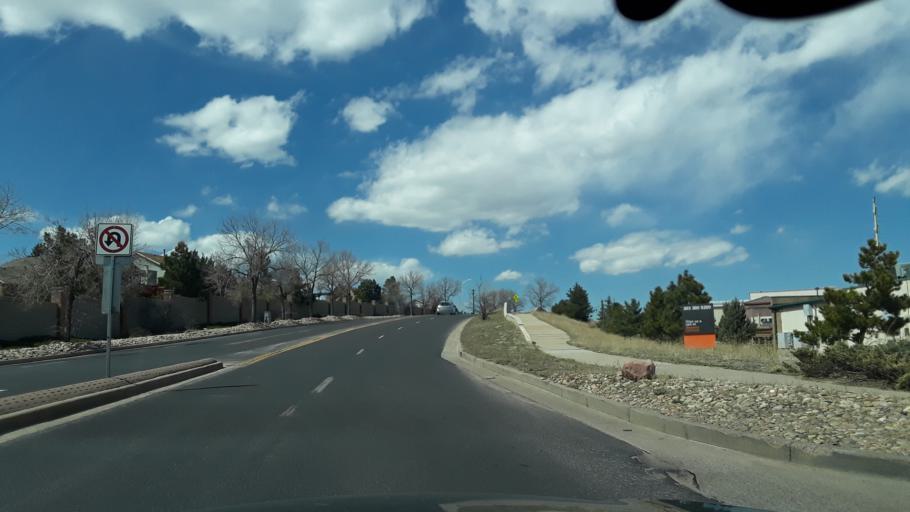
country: US
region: Colorado
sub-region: El Paso County
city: Black Forest
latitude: 38.9384
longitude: -104.7624
